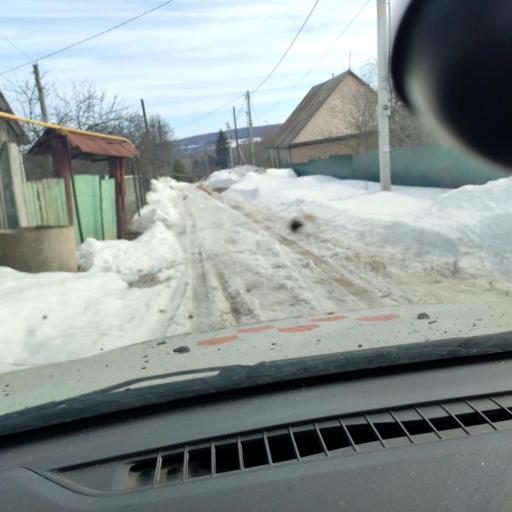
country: RU
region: Bashkortostan
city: Avdon
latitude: 54.6211
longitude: 55.6477
